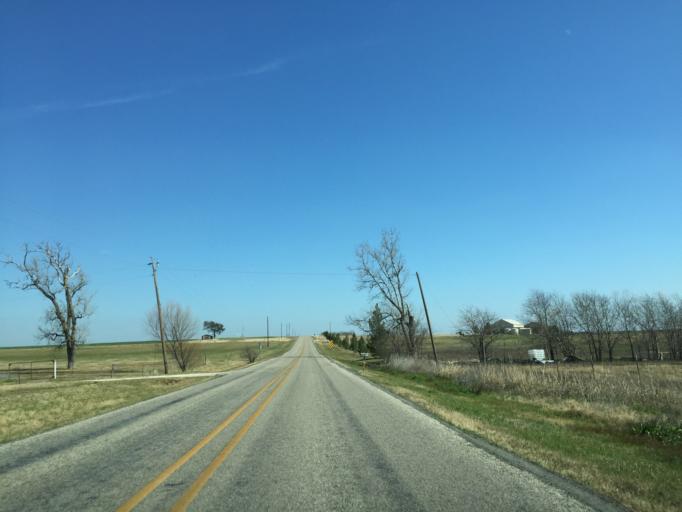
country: US
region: Texas
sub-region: Williamson County
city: Granger
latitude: 30.7546
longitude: -97.5414
